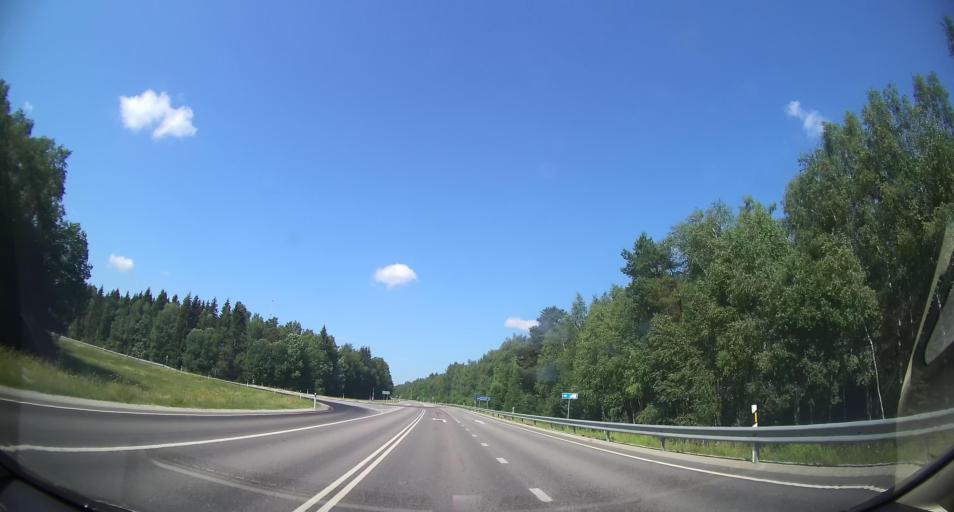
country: EE
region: Raplamaa
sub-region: Rapla vald
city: Rapla
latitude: 59.0205
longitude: 24.7844
